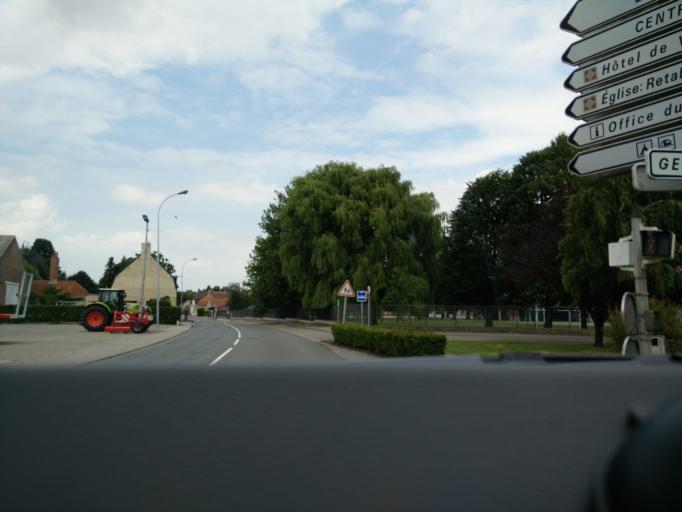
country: FR
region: Nord-Pas-de-Calais
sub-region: Departement du Nord
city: Hondschoote
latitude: 50.9768
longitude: 2.5809
